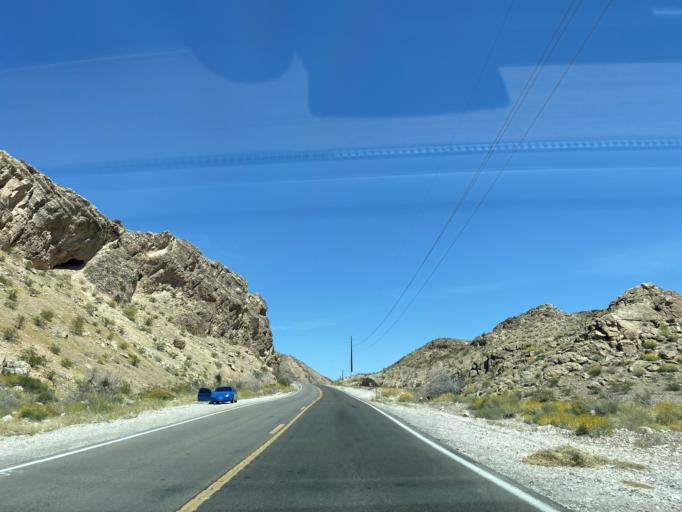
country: US
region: Nevada
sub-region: Clark County
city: Nellis Air Force Base
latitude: 36.2001
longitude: -114.9972
